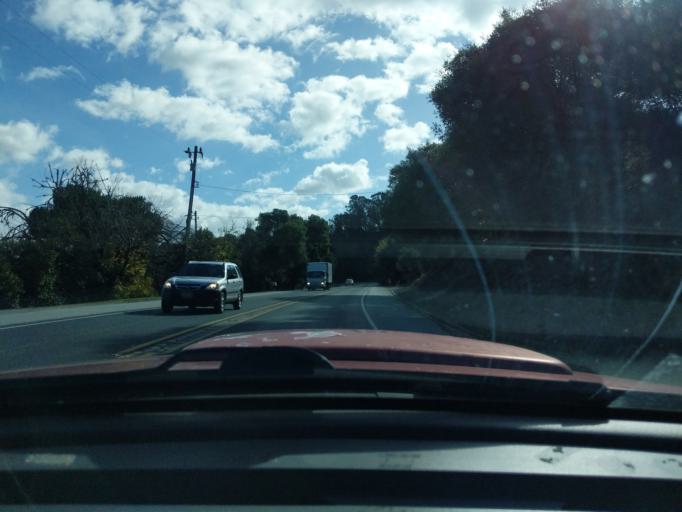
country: US
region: California
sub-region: San Benito County
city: Aromas
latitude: 36.8954
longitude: -121.5801
